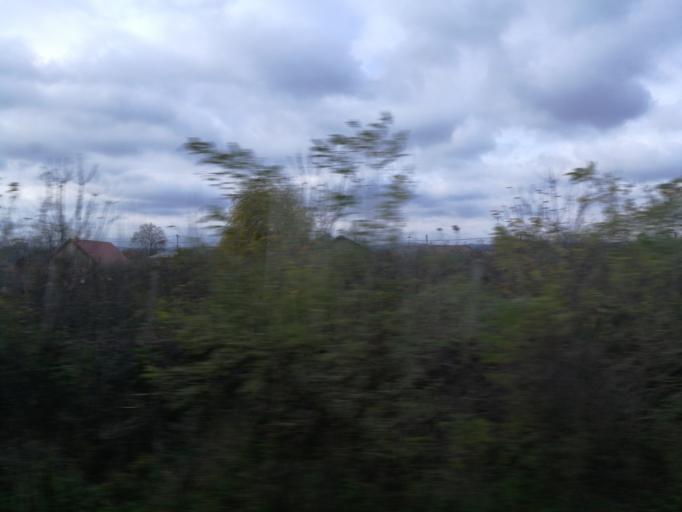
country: RO
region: Bacau
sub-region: Comuna Sascut
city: Sascut
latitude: 46.2185
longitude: 27.1031
